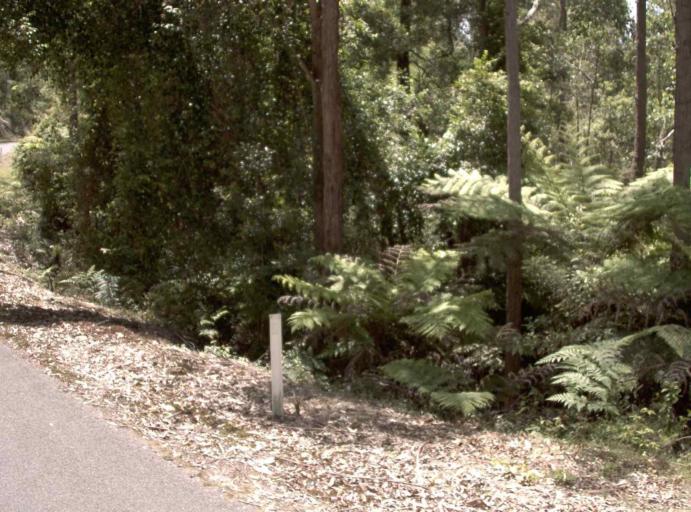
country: AU
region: New South Wales
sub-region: Bombala
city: Bombala
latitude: -37.5050
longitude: 148.9248
